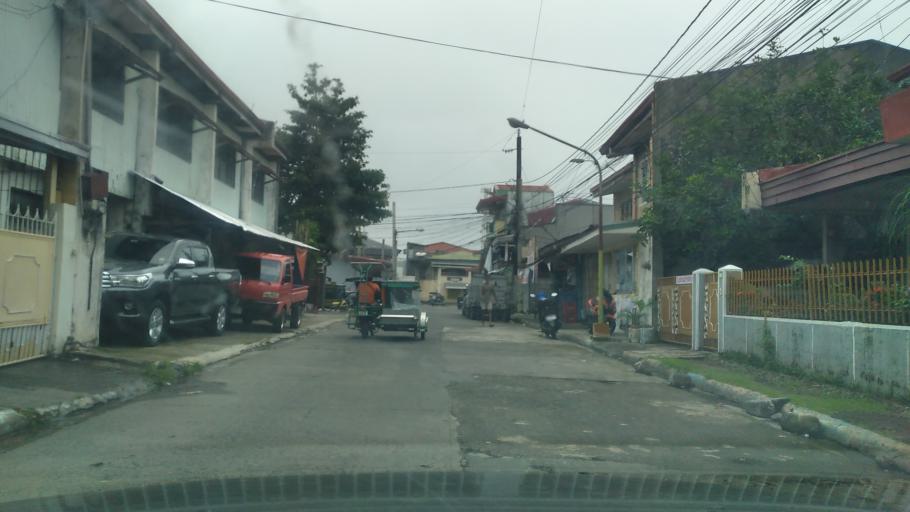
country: PH
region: Calabarzon
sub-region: Province of Quezon
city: Lucena
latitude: 13.9354
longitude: 121.6164
